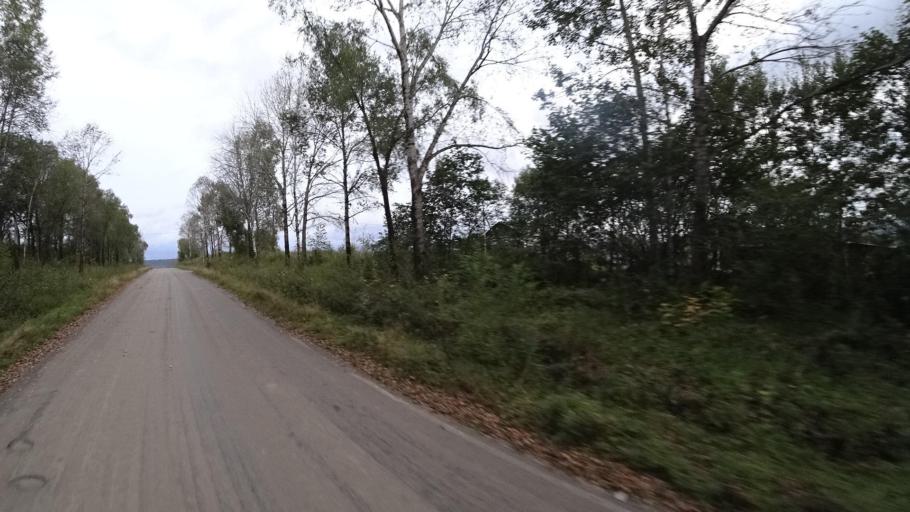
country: RU
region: Jewish Autonomous Oblast
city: Izvestkovyy
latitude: 48.9757
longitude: 131.5720
